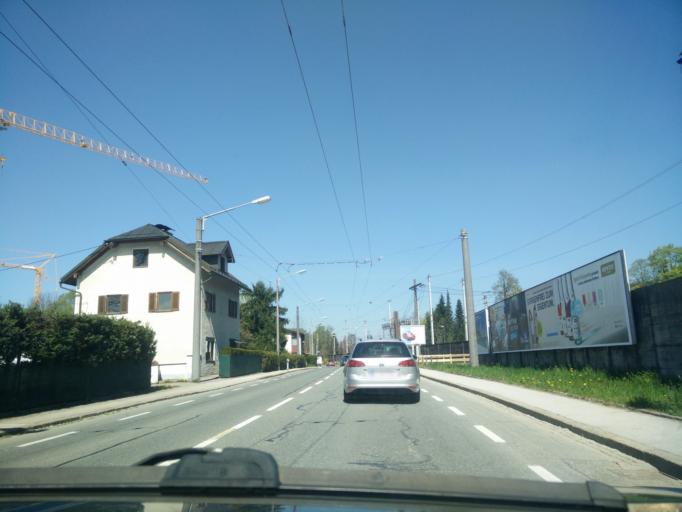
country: AT
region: Salzburg
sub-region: Politischer Bezirk Salzburg-Umgebung
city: Elsbethen
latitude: 47.7867
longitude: 13.0799
